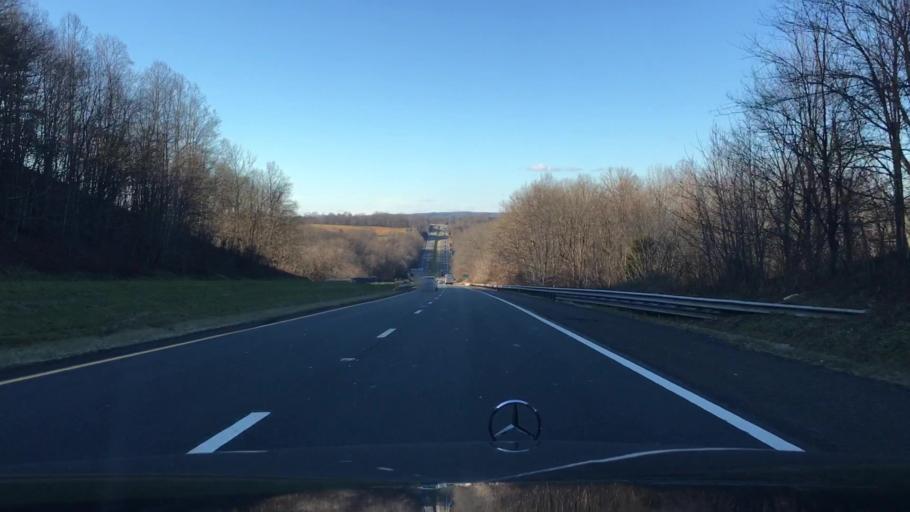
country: US
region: Virginia
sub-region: Montgomery County
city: Christiansburg
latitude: 37.1404
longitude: -80.3834
